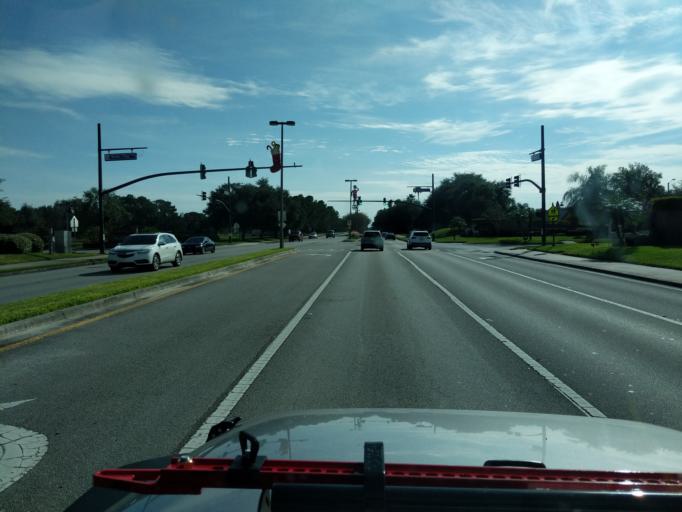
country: US
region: Florida
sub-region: Orange County
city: Gotha
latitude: 28.5388
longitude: -81.5420
